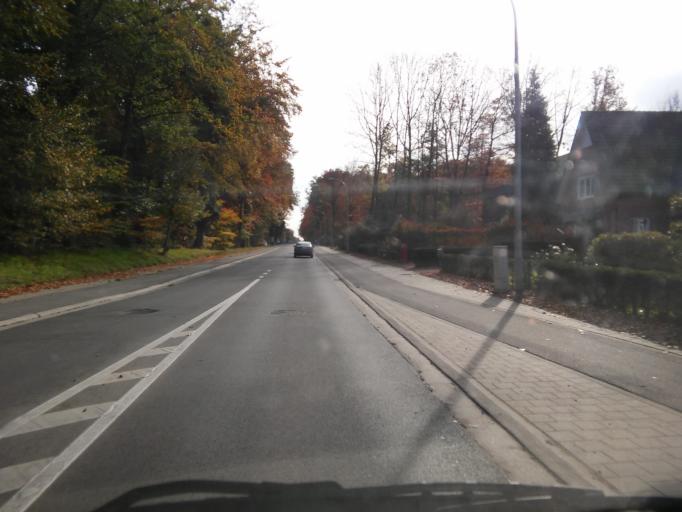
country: BE
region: Flanders
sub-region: Provincie Oost-Vlaanderen
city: Buggenhout
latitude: 51.0042
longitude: 4.2080
